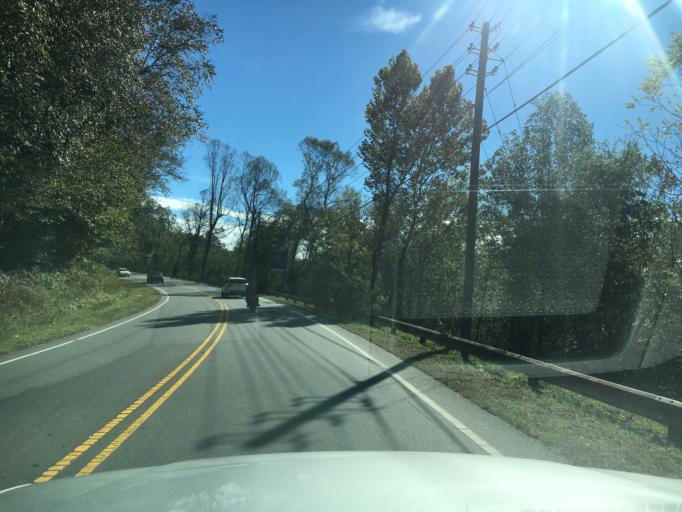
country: US
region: North Carolina
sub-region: Burke County
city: Morganton
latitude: 35.7523
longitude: -81.7056
